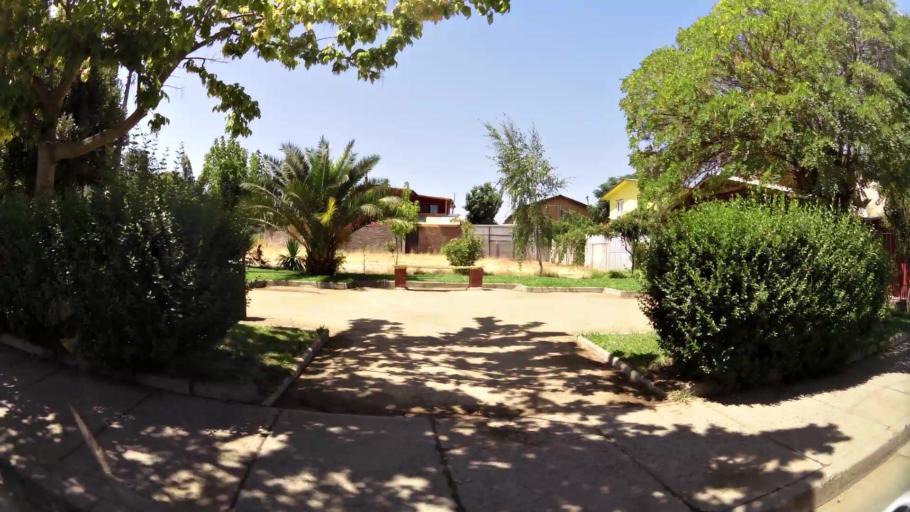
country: CL
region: Maule
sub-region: Provincia de Talca
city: Talca
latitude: -35.4367
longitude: -71.6340
